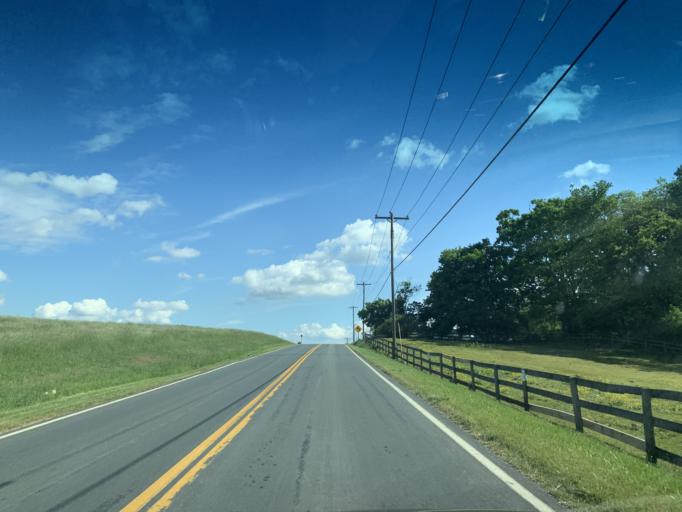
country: US
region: Maryland
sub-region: Cecil County
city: Rising Sun
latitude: 39.7034
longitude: -76.1451
